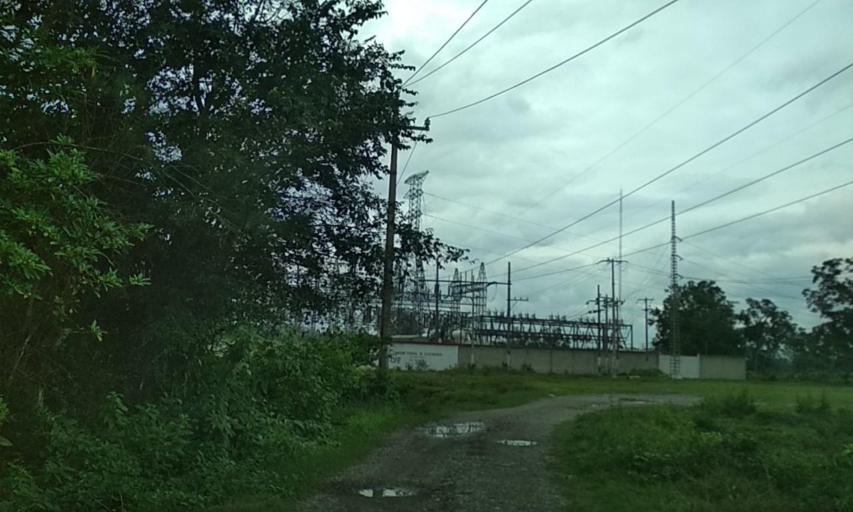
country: MX
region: Veracruz
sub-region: Papantla
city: El Chote
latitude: 20.3946
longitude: -97.3368
